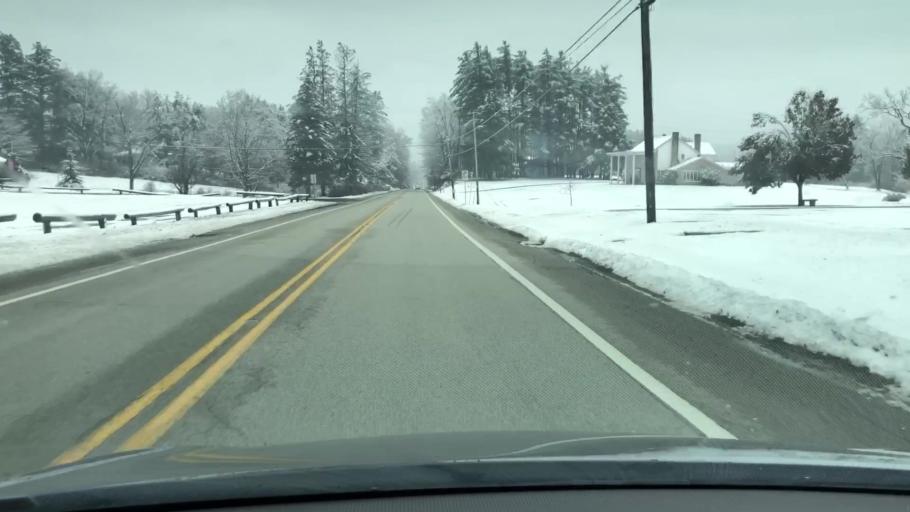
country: US
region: Pennsylvania
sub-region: Fayette County
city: Hopwood
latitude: 39.8301
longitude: -79.5989
